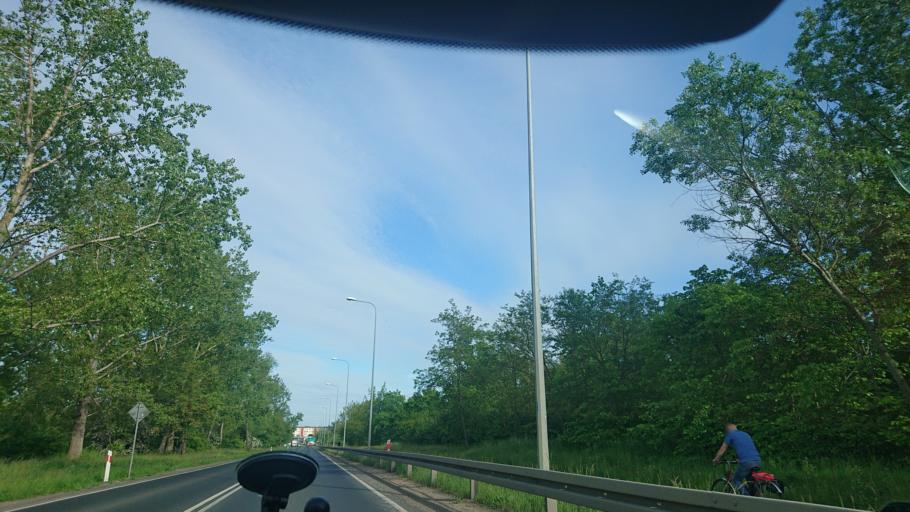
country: PL
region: Greater Poland Voivodeship
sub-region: Powiat gnieznienski
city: Gniezno
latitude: 52.5156
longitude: 17.5872
